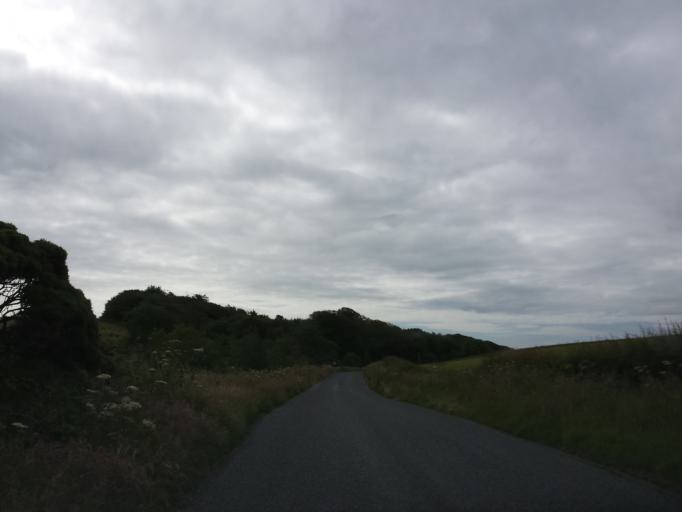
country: GB
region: Scotland
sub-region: Dumfries and Galloway
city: Stranraer
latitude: 54.8625
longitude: -5.1064
